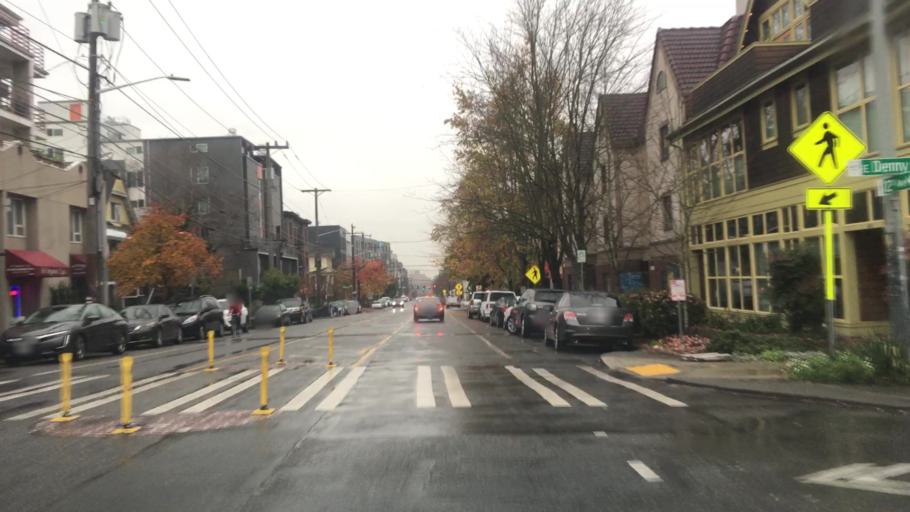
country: US
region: Washington
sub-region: King County
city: Seattle
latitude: 47.6188
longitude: -122.3170
